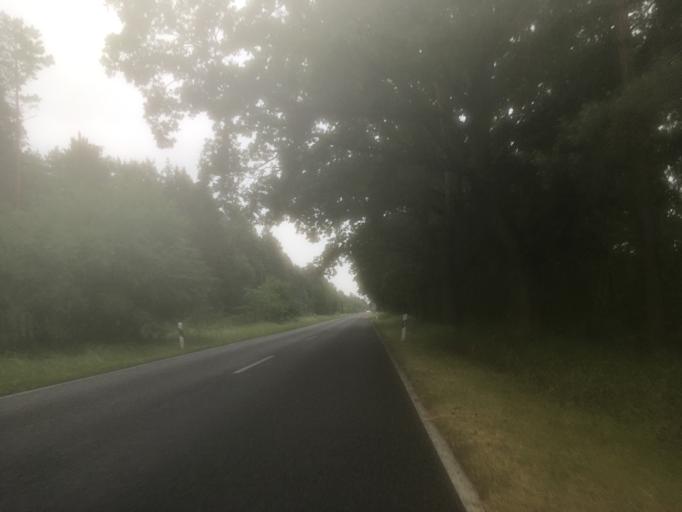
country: DE
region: Brandenburg
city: Zehdenick
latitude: 53.0129
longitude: 13.3421
